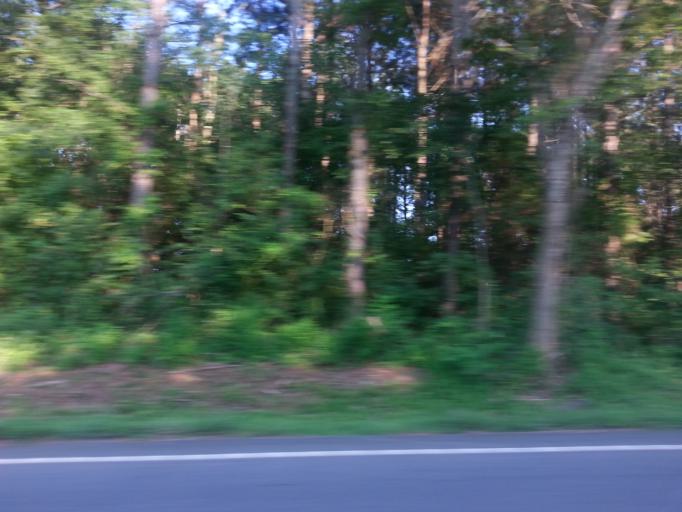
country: US
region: Tennessee
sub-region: Monroe County
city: Sweetwater
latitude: 35.5422
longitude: -84.5202
